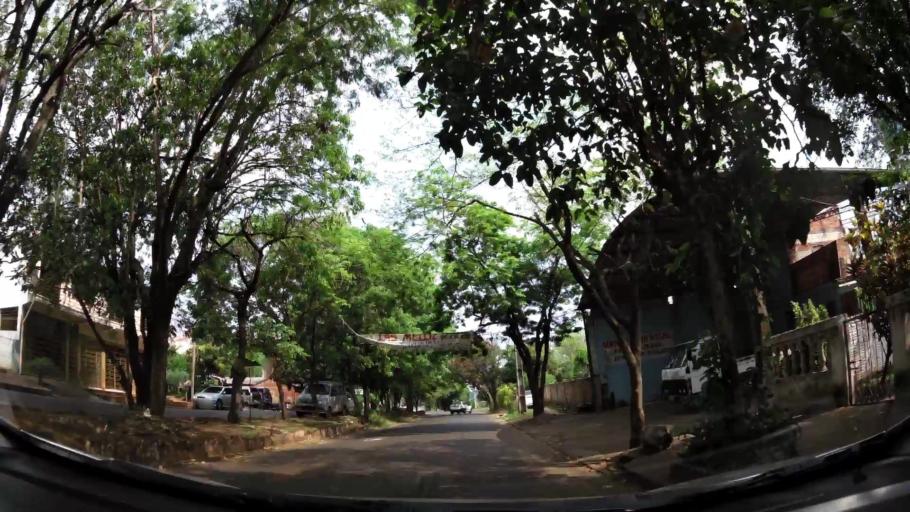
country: PY
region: Alto Parana
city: Presidente Franco
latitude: -25.5386
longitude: -54.6063
